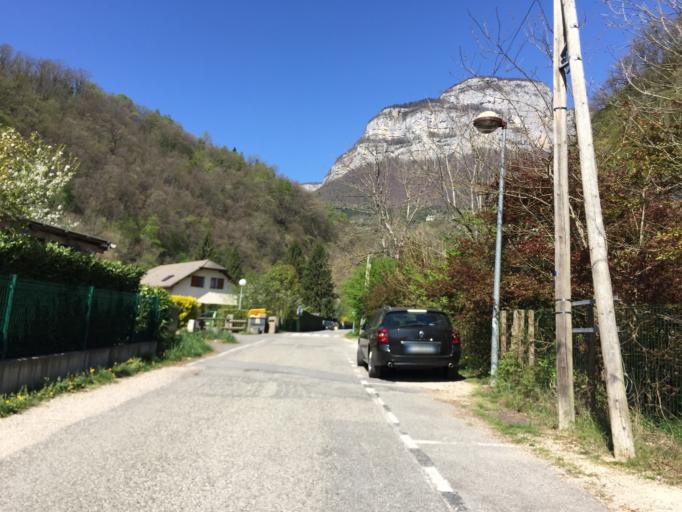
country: FR
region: Rhone-Alpes
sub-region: Departement de la Savoie
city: Barby
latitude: 45.5792
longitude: 5.9749
